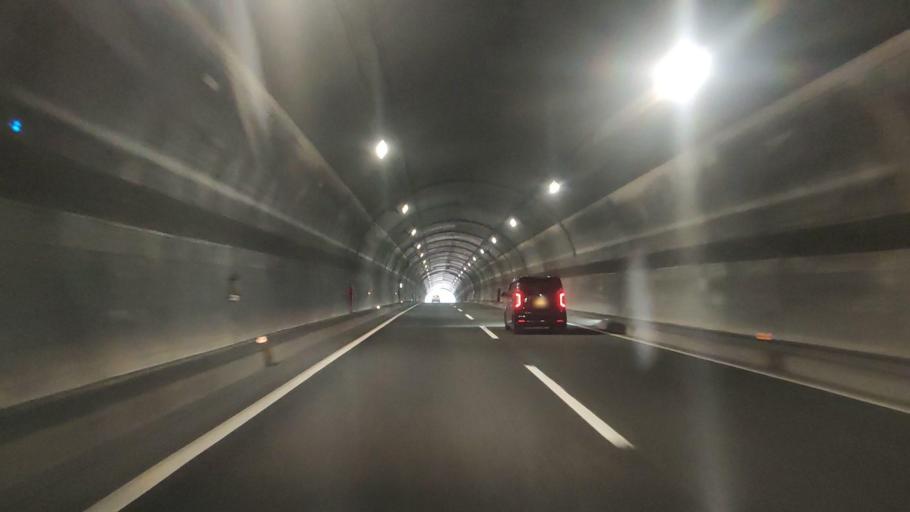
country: JP
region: Yamaguchi
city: Shimonoseki
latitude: 33.9184
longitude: 130.9657
